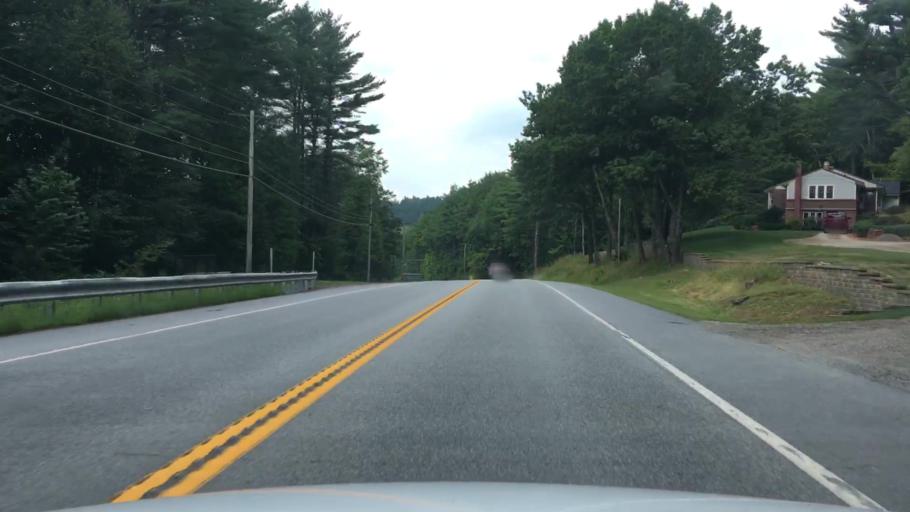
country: US
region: Maine
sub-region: Oxford County
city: Rumford
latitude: 44.5102
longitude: -70.6075
